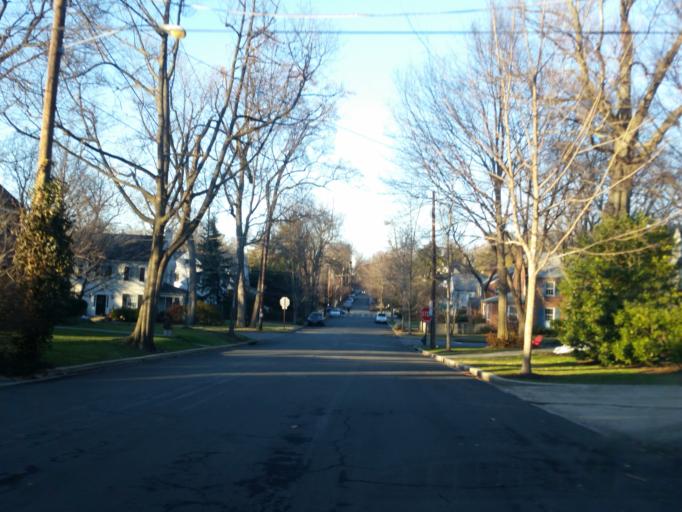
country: US
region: Maryland
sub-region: Montgomery County
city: Friendship Village
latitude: 38.9483
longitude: -77.0926
